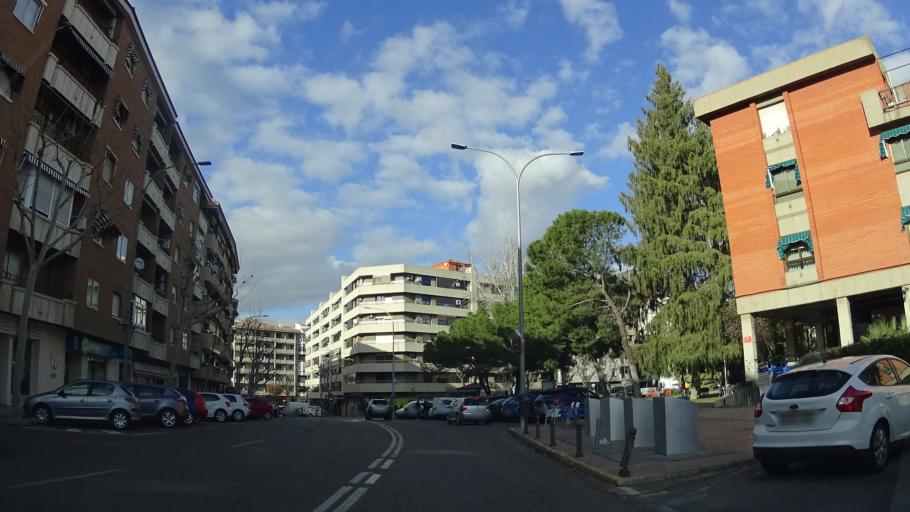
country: ES
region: Castille-La Mancha
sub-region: Provincia de Ciudad Real
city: Ciudad Real
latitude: 38.9835
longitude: -3.9253
